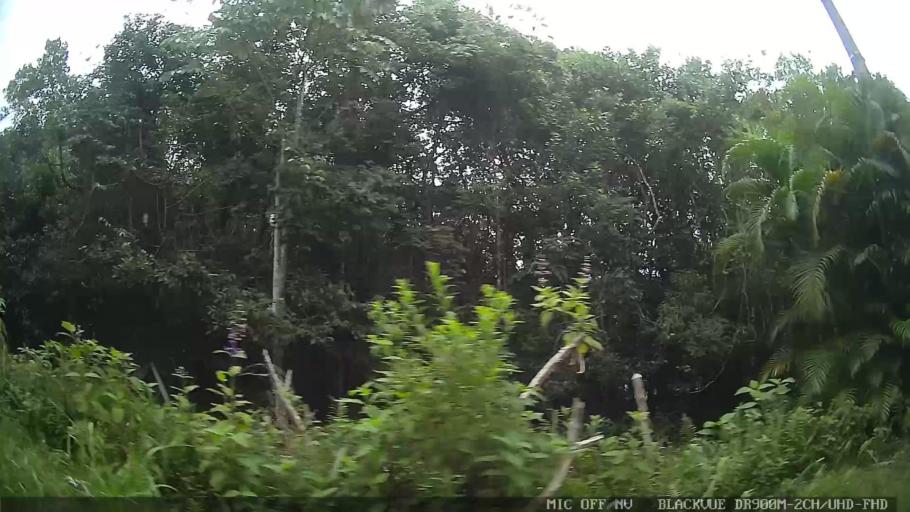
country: BR
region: Sao Paulo
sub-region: Iguape
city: Iguape
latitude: -24.6870
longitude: -47.5115
